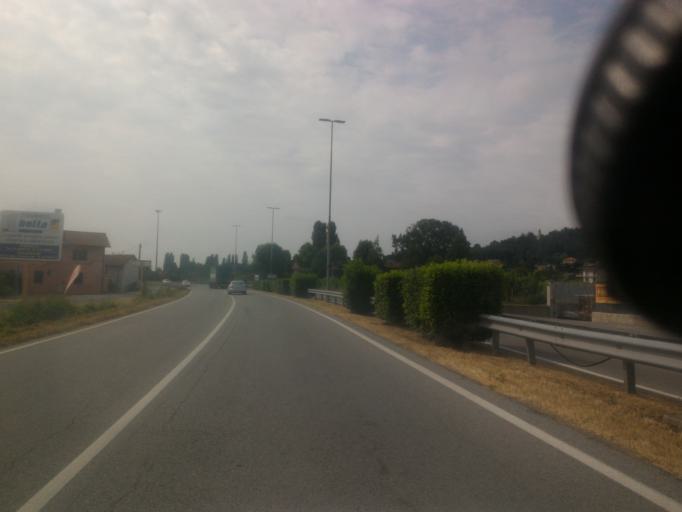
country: IT
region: Piedmont
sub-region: Provincia di Torino
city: Bricherasio
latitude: 44.8343
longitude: 7.3051
